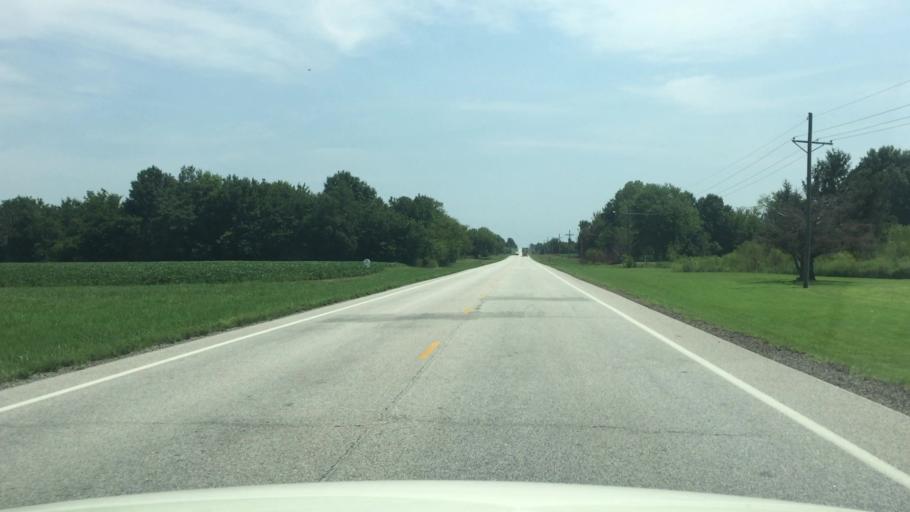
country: US
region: Kansas
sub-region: Cherokee County
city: Columbus
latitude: 37.1781
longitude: -94.8076
